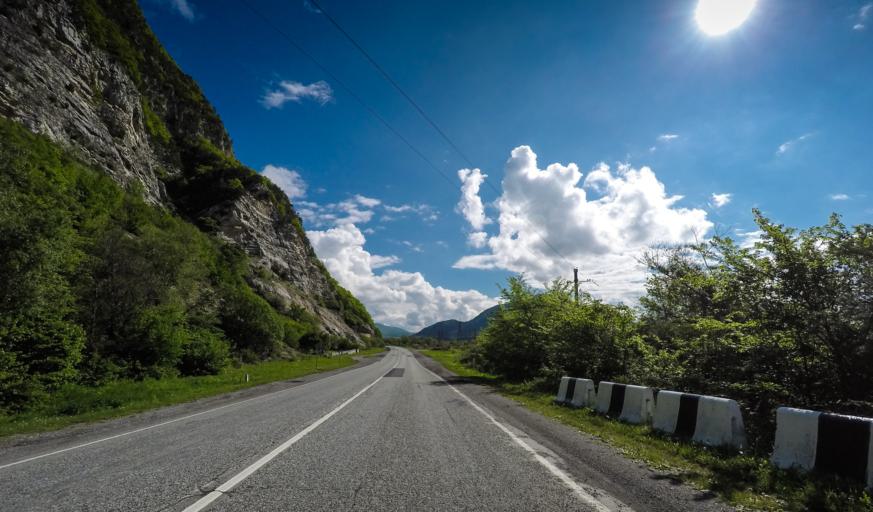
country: RU
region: North Ossetia
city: Vladikavkaz
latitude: 42.9375
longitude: 44.6500
